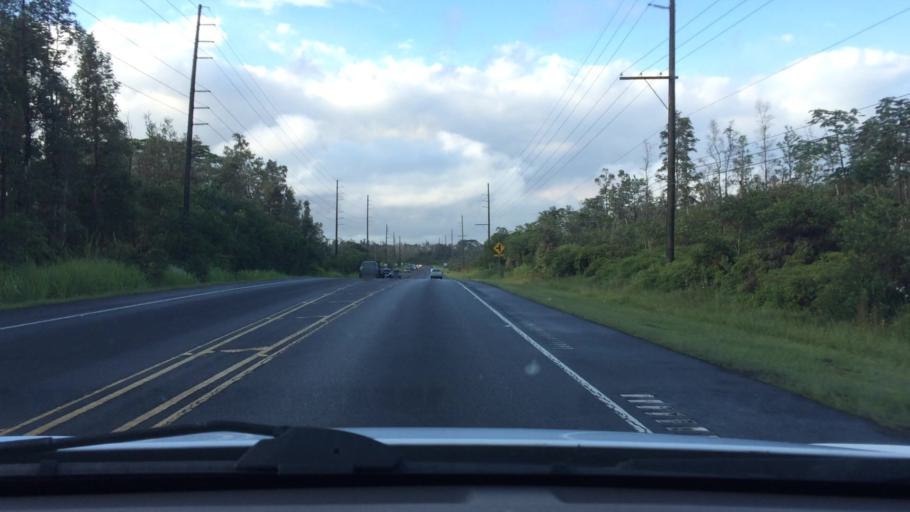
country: US
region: Hawaii
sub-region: Hawaii County
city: Ainaloa
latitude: 19.5325
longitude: -154.9716
